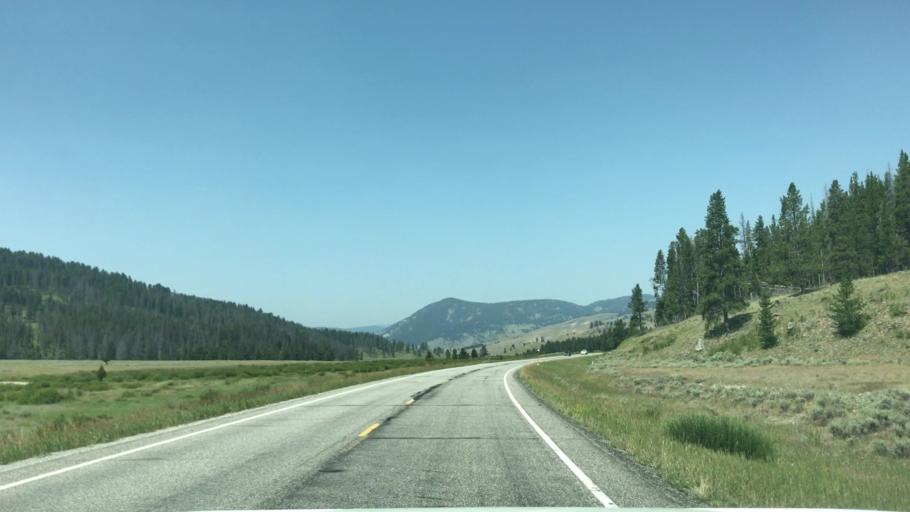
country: US
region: Montana
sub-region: Gallatin County
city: Big Sky
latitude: 45.0286
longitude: -111.1079
